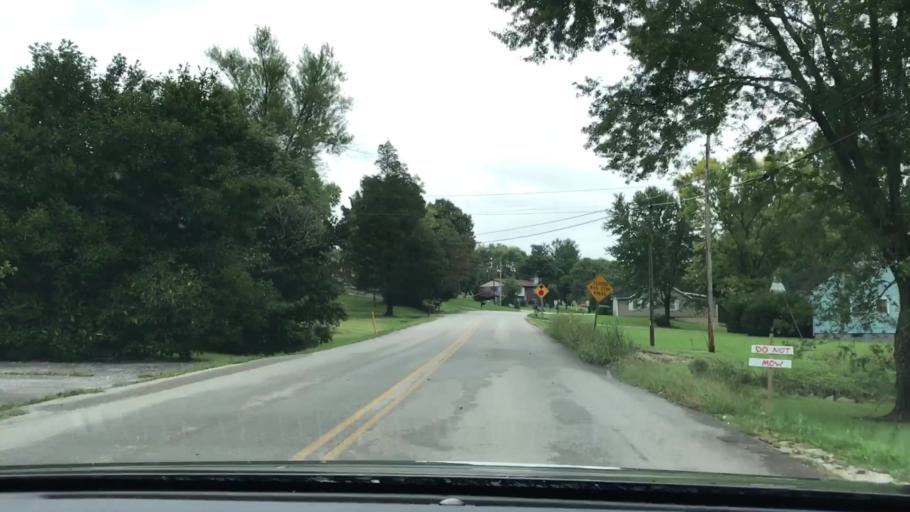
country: US
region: Kentucky
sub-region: Barren County
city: Glasgow
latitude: 36.9629
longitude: -85.8680
